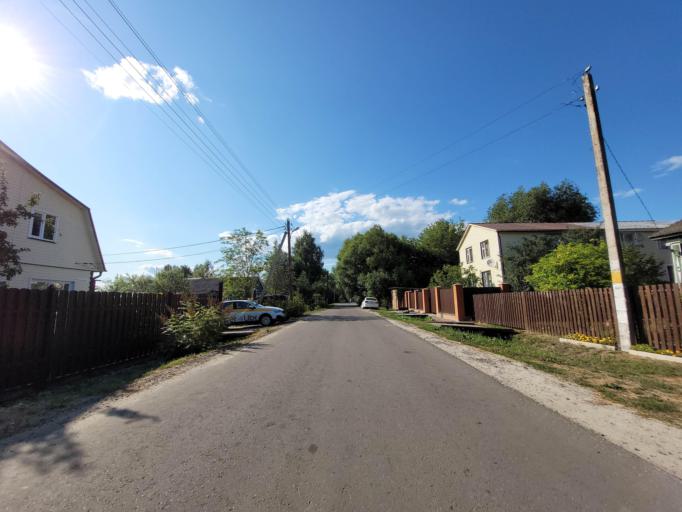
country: RU
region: Moskovskaya
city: Konobeyevo
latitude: 55.4103
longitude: 38.6984
